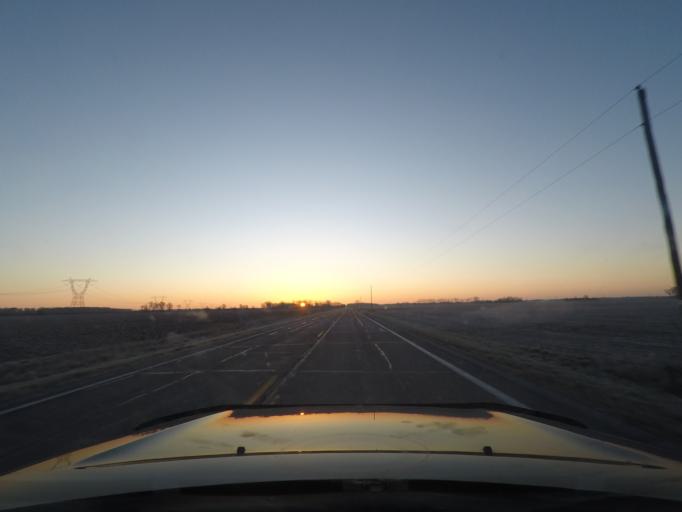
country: US
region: Indiana
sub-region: LaPorte County
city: Fish Lake
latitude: 41.4764
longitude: -86.5779
